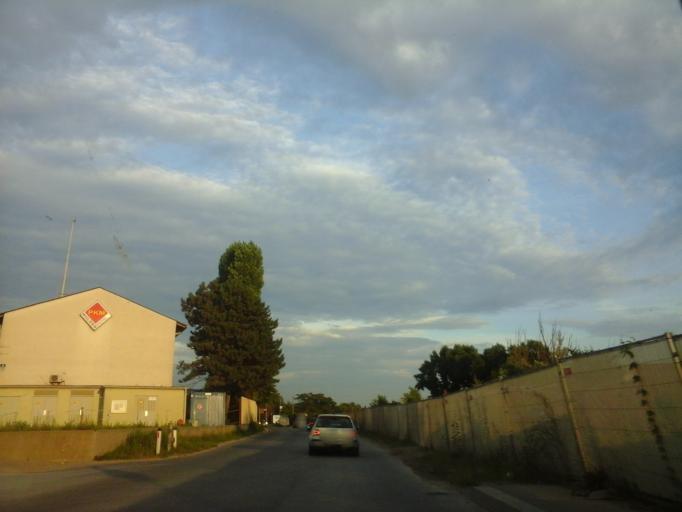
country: AT
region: Lower Austria
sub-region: Politischer Bezirk Wien-Umgebung
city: Schwechat
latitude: 48.1732
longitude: 16.4706
